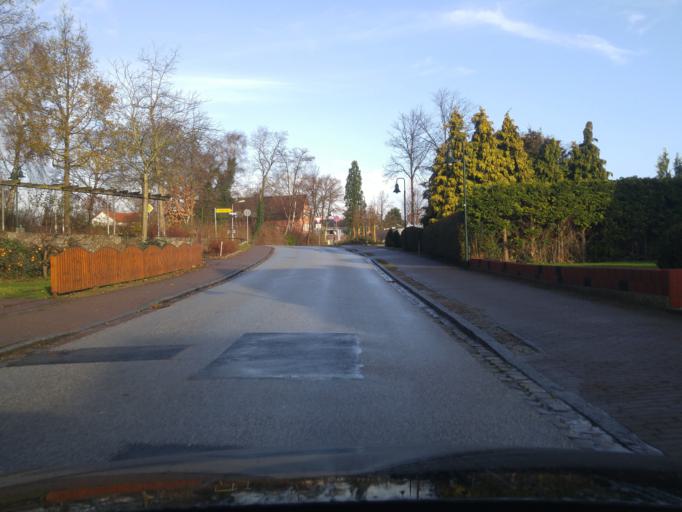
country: DE
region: Schleswig-Holstein
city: Ratekau
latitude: 53.9443
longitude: 10.7330
